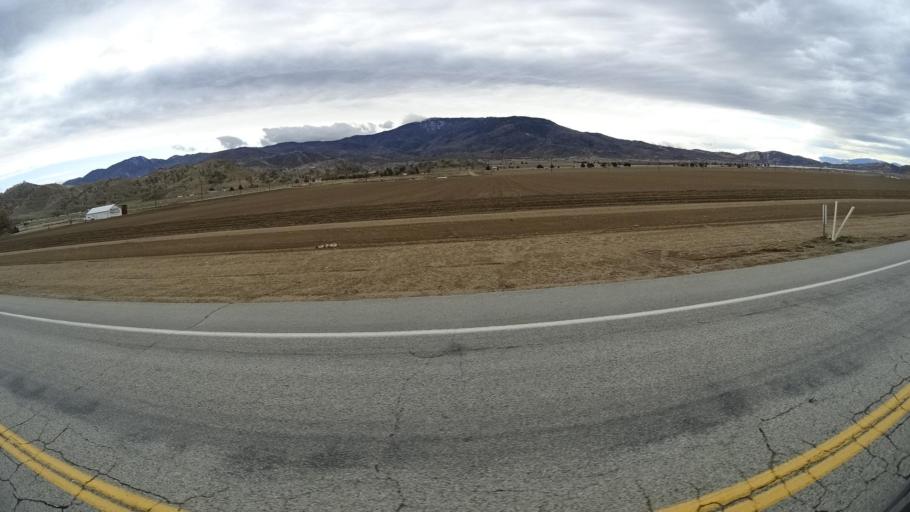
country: US
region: California
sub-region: Kern County
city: Bear Valley Springs
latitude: 35.1310
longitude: -118.5766
